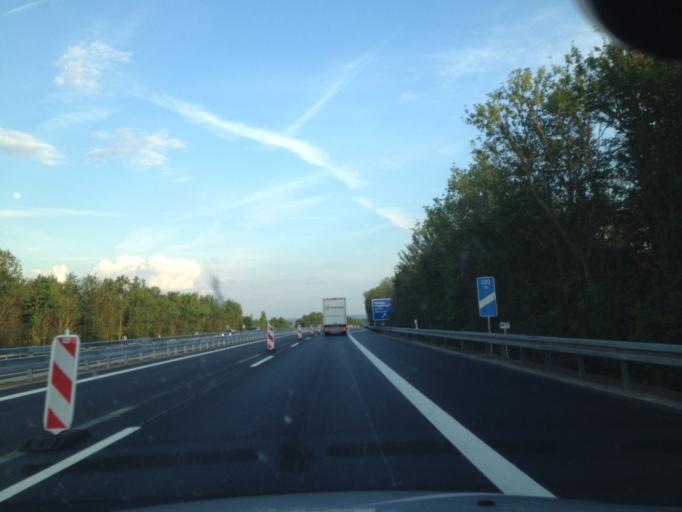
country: DE
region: Bavaria
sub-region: Regierungsbezirk Unterfranken
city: Biebelried
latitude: 49.7632
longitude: 10.1037
